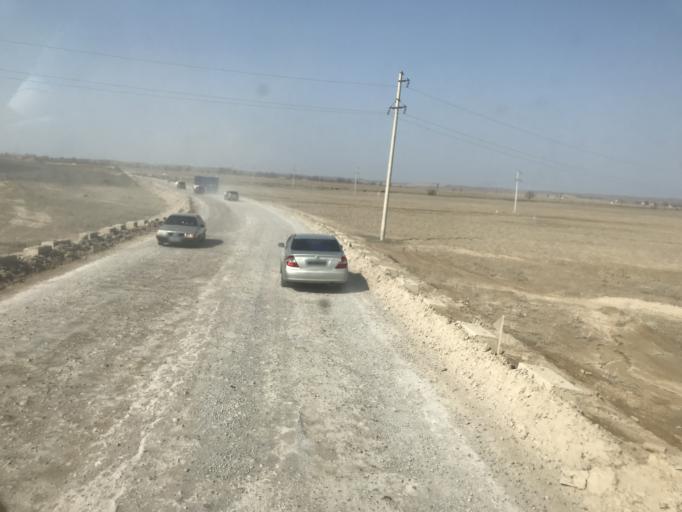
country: KG
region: Chuy
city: Bystrovka
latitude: 43.3226
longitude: 76.0410
